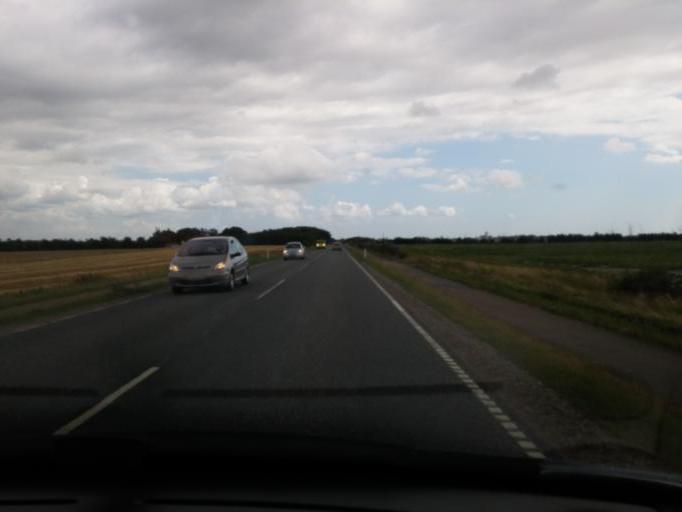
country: DK
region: South Denmark
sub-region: Langeland Kommune
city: Rudkobing
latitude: 54.9567
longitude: 10.6808
